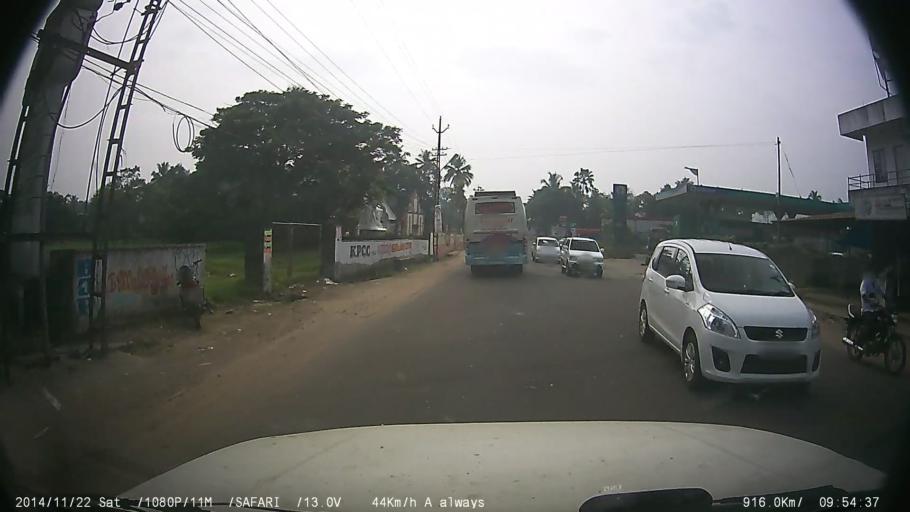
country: IN
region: Kerala
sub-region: Ernakulam
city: Perumpavur
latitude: 10.1097
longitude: 76.4802
